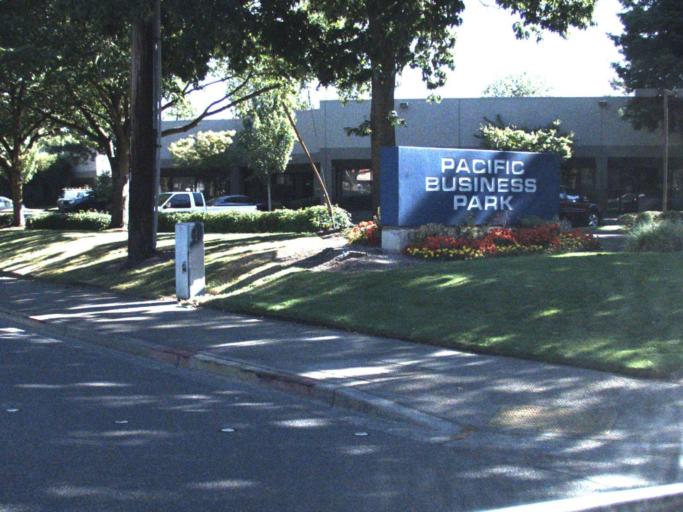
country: US
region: Washington
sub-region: King County
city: Kent
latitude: 47.4051
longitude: -122.2494
